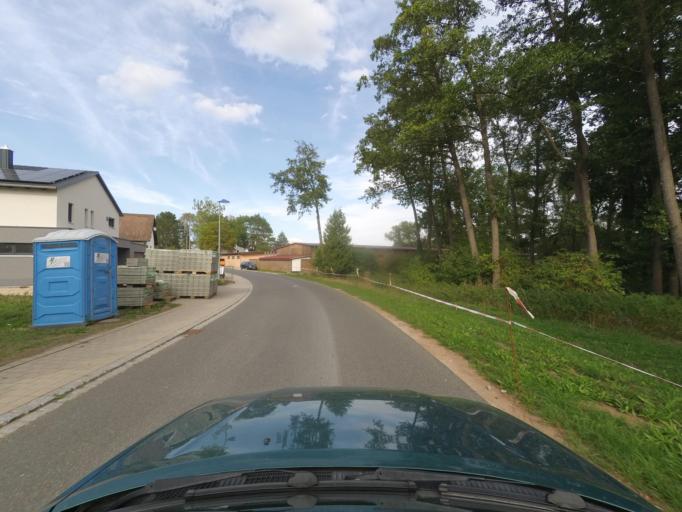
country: DE
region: Bavaria
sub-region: Upper Palatinate
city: Freystadt
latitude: 49.2397
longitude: 11.2966
